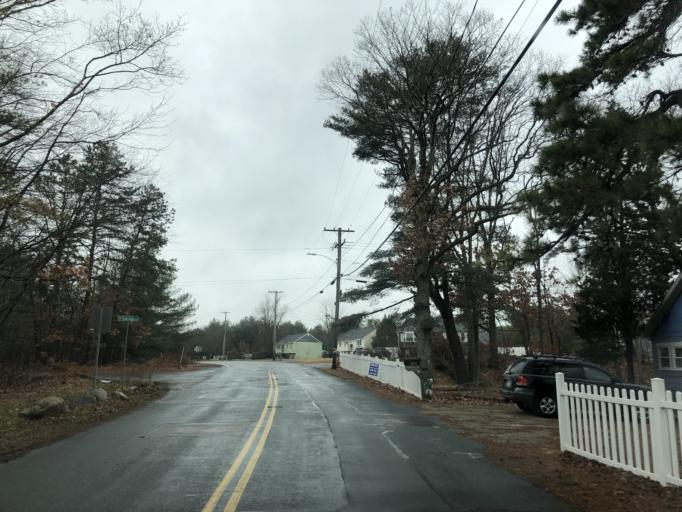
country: US
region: Massachusetts
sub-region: Norfolk County
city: Plainville
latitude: 42.0056
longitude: -71.2807
